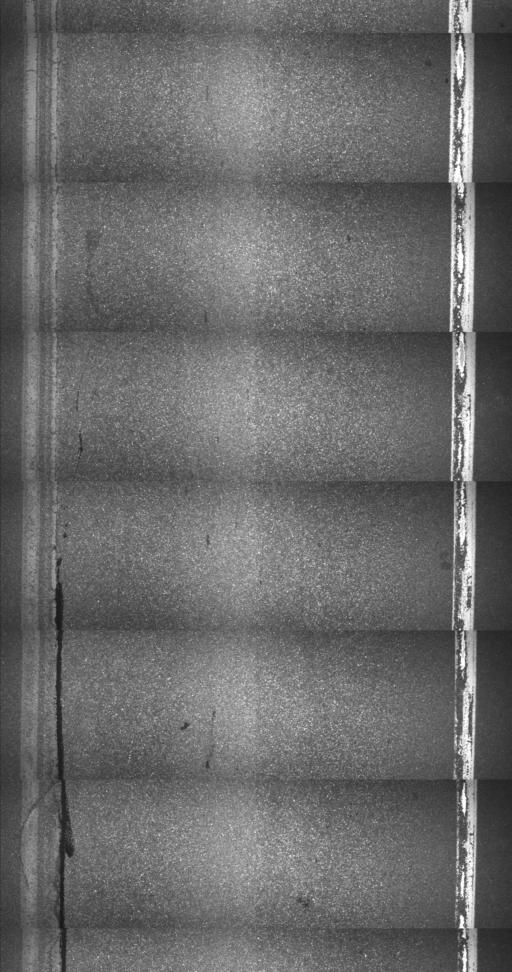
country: US
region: Vermont
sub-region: Orleans County
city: Newport
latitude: 44.9316
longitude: -72.2548
